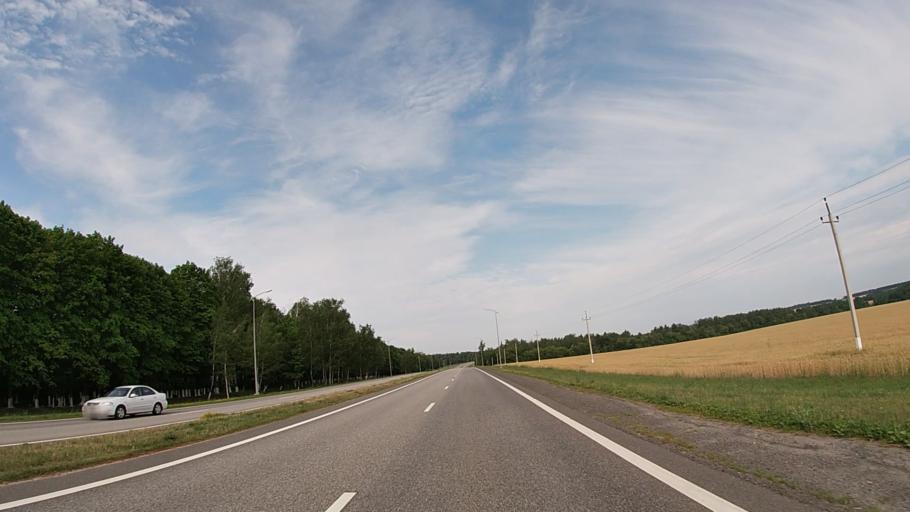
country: RU
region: Belgorod
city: Borisovka
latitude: 50.7507
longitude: 36.0018
